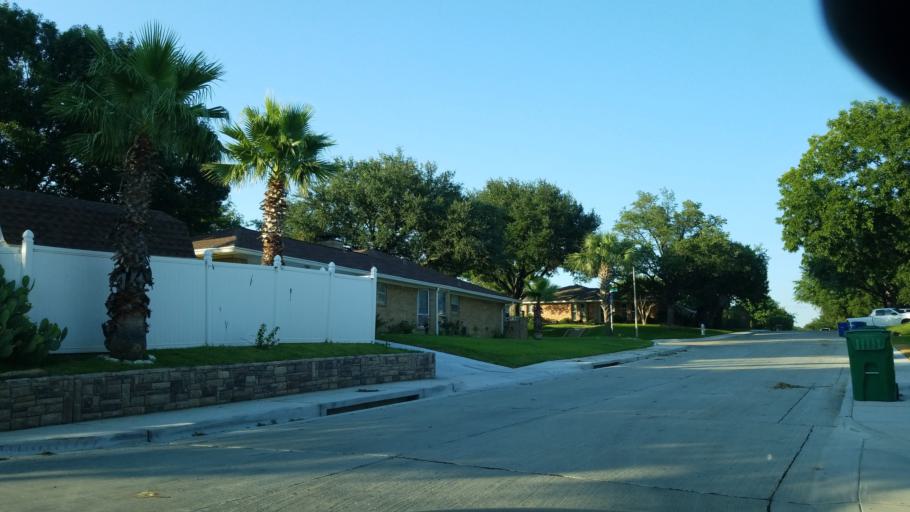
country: US
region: Texas
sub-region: Dallas County
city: Carrollton
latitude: 32.9598
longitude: -96.9006
